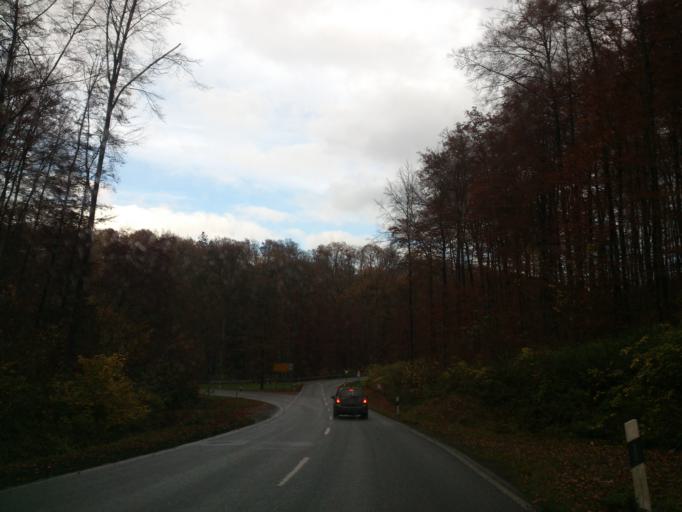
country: DE
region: Lower Saxony
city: Boffzen
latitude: 51.7522
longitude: 9.2861
